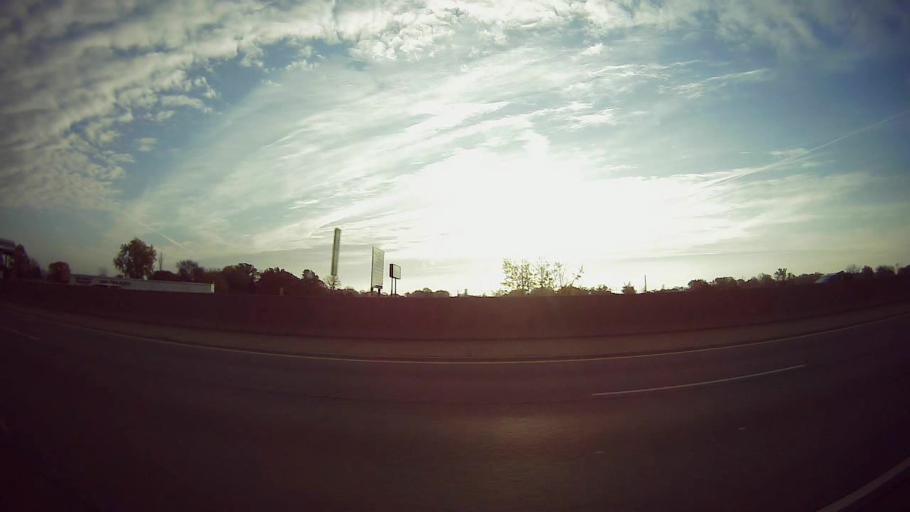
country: US
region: Michigan
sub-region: Macomb County
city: Saint Clair Shores
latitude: 42.5427
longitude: -82.8833
